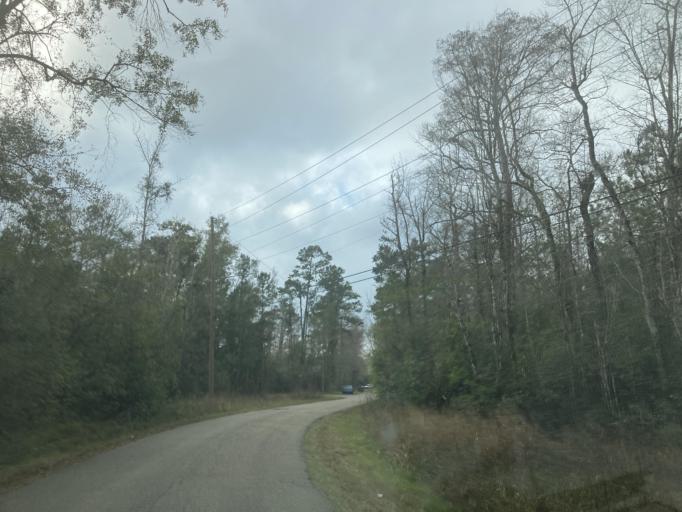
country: US
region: Mississippi
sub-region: Harrison County
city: West Gulfport
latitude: 30.4774
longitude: -89.0162
